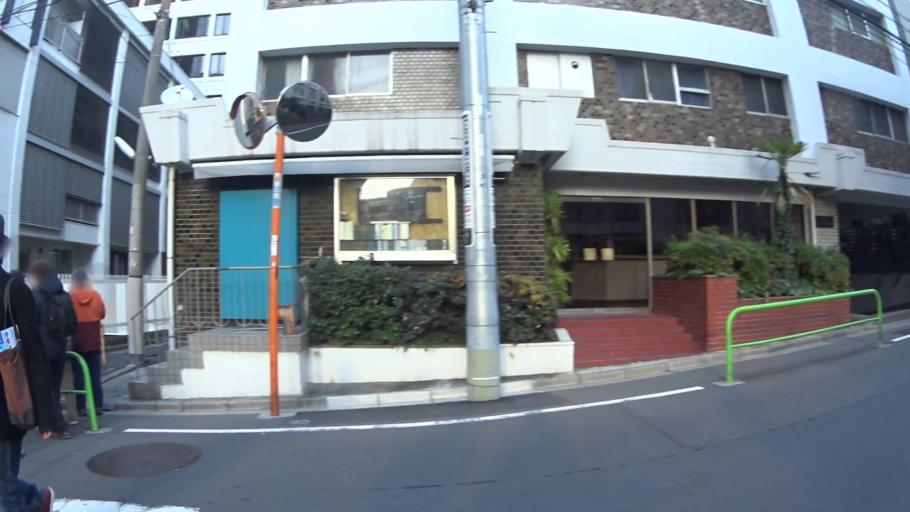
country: JP
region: Tokyo
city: Tokyo
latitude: 35.6696
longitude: 139.7353
